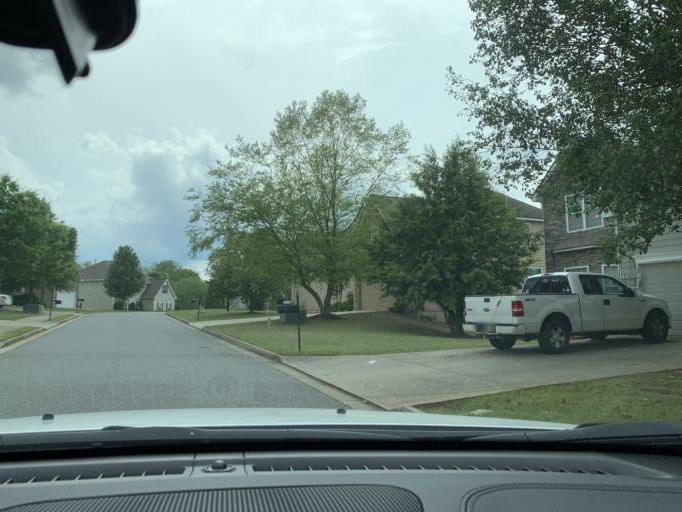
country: US
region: Georgia
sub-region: Gwinnett County
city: Suwanee
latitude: 34.1179
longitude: -84.1176
